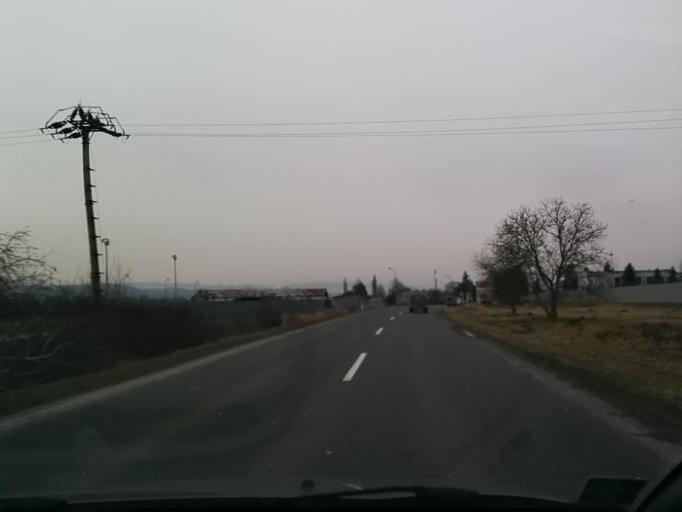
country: SK
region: Banskobystricky
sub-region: Okres Banska Bystrica
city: Zvolen
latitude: 48.6441
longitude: 19.1414
